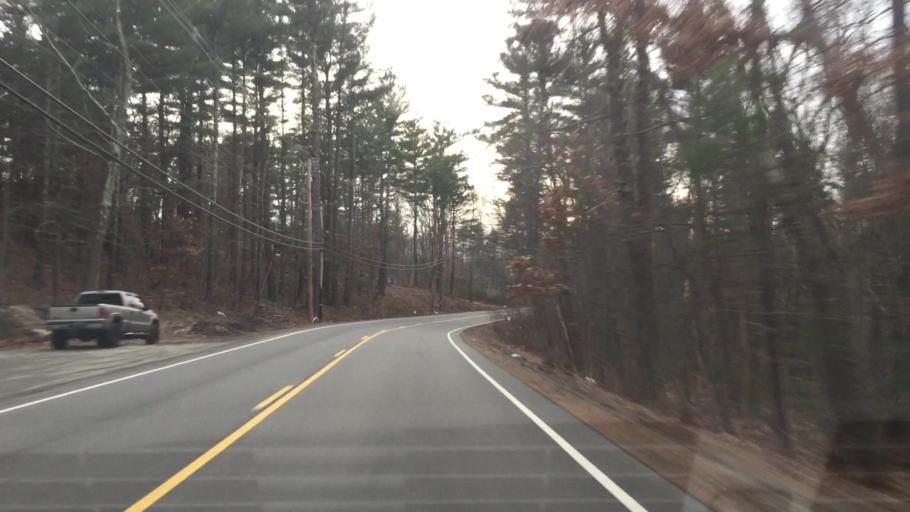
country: US
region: New Hampshire
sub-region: Hillsborough County
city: Pelham
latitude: 42.7486
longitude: -71.2734
